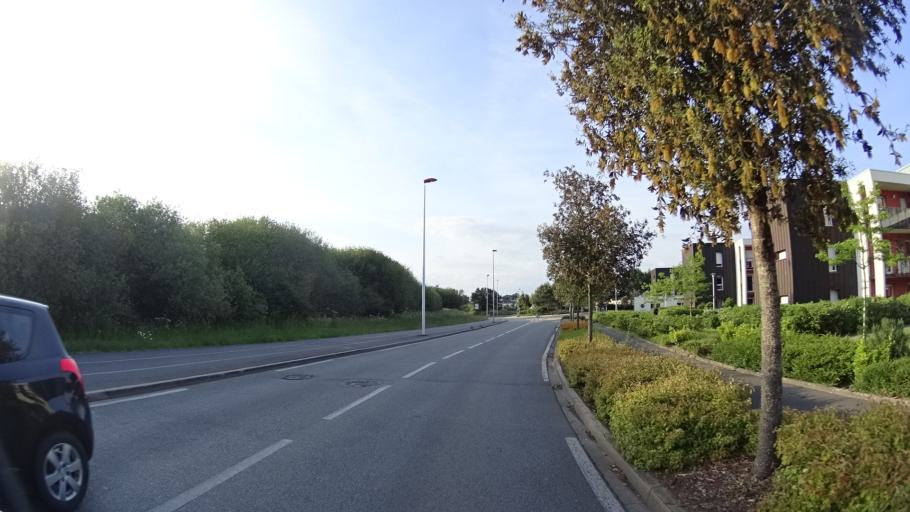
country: FR
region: Brittany
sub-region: Departement du Morbihan
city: Vannes
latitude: 47.6484
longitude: -2.7442
